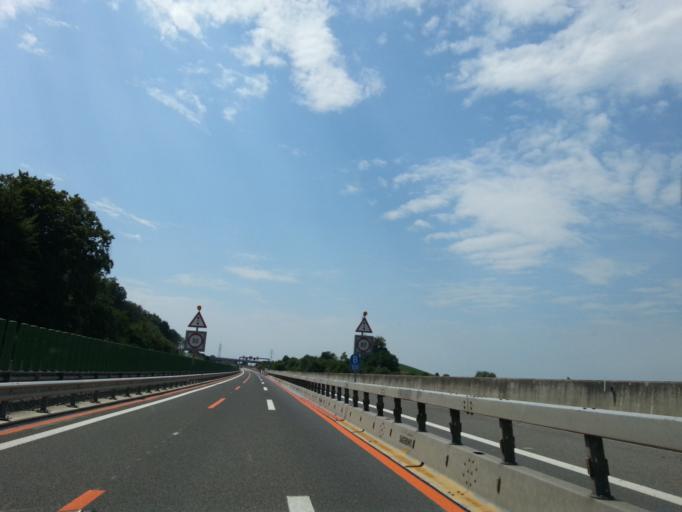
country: CH
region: Fribourg
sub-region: See District
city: Murten
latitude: 46.9373
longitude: 7.1440
